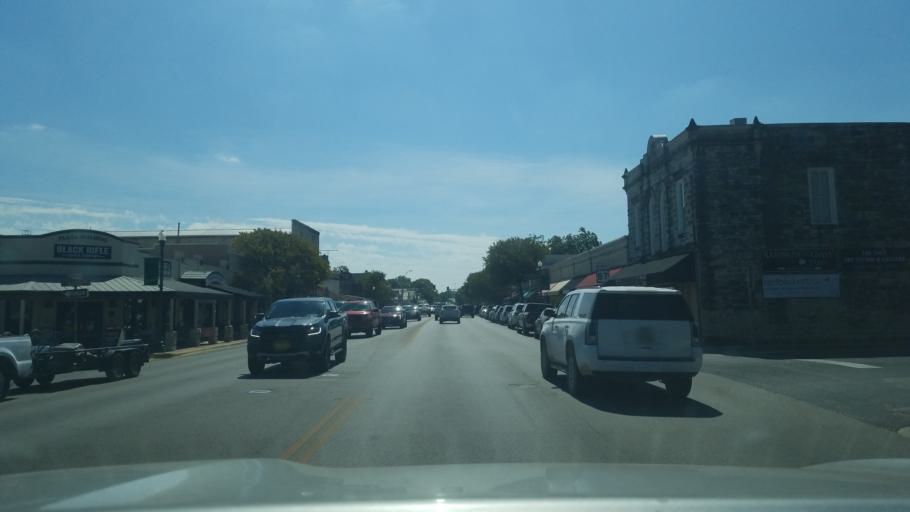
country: US
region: Texas
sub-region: Kendall County
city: Boerne
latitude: 29.7941
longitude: -98.7320
